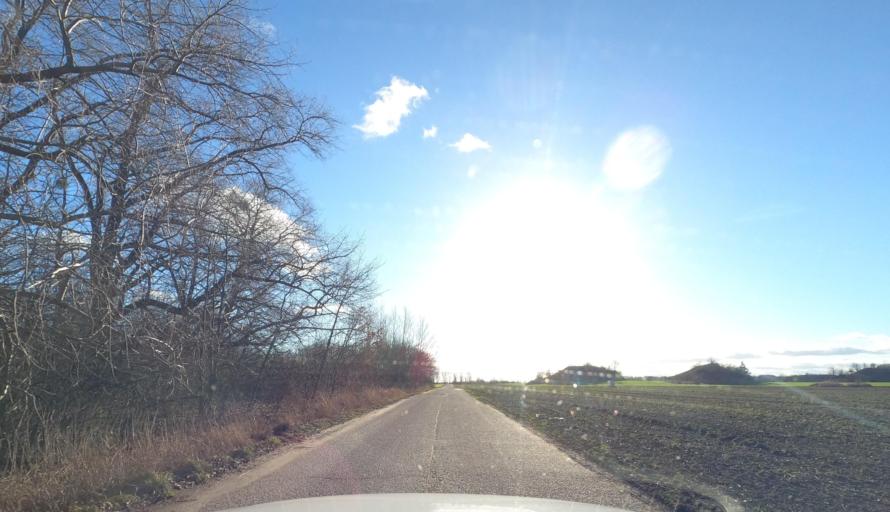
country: PL
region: West Pomeranian Voivodeship
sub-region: Powiat pyrzycki
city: Warnice
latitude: 53.2903
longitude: 14.9923
